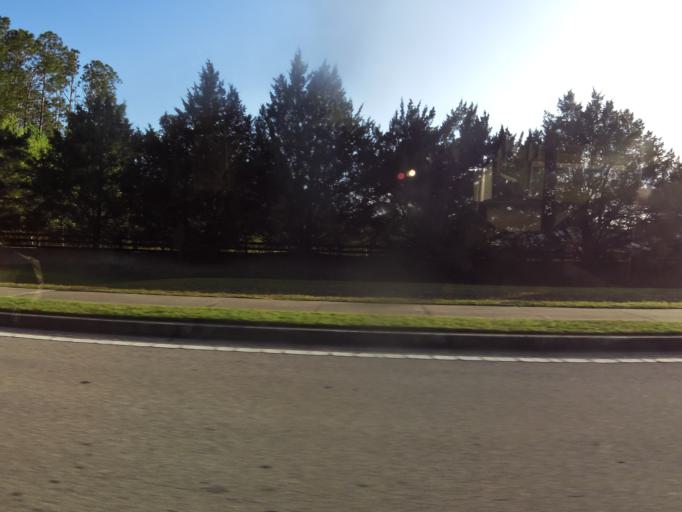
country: US
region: Florida
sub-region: Saint Johns County
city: Fruit Cove
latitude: 30.0729
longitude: -81.5156
